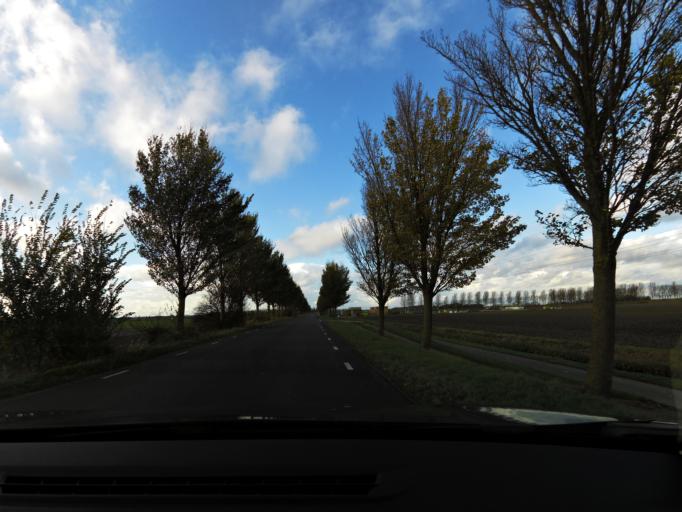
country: NL
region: South Holland
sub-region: Gemeente Goeree-Overflakkee
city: Middelharnis
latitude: 51.7433
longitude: 4.2050
